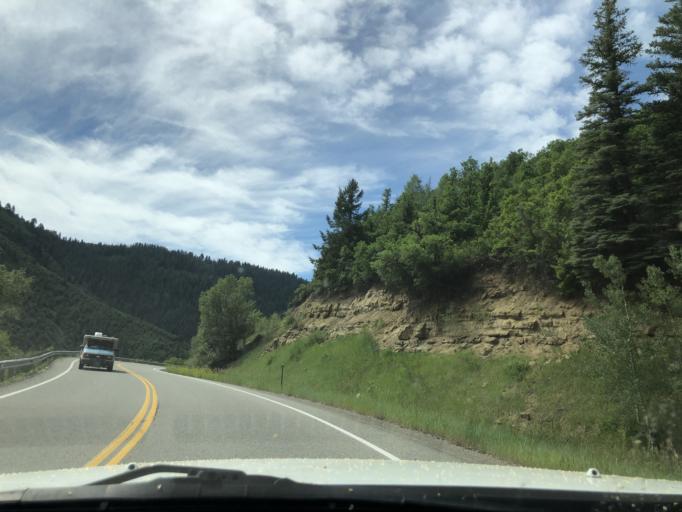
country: US
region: Colorado
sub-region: Delta County
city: Paonia
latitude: 38.9560
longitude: -107.3439
